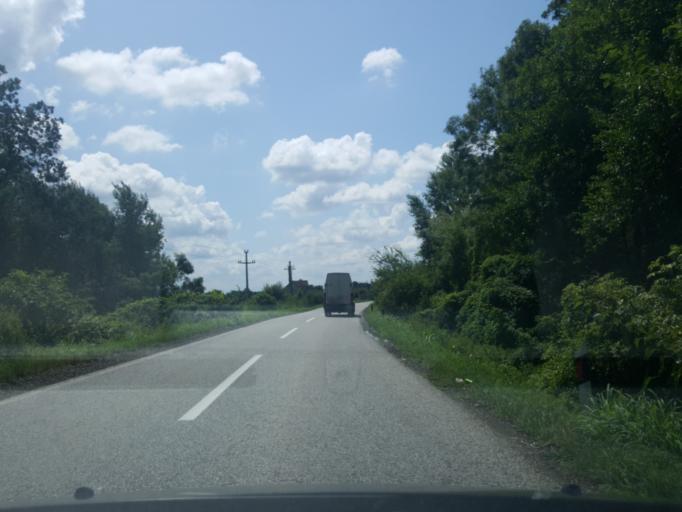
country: RS
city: Glusci
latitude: 44.9028
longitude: 19.5465
